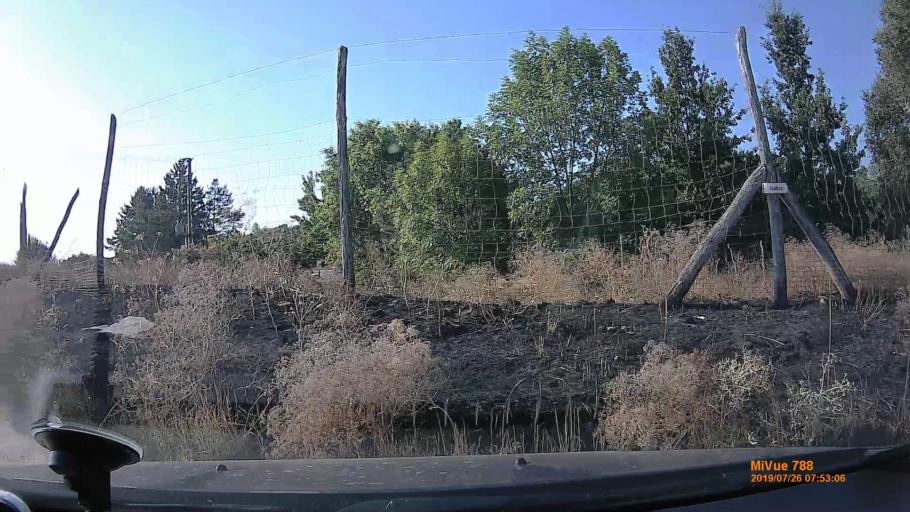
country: HU
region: Pest
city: Mogyorod
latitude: 47.5938
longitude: 19.2179
